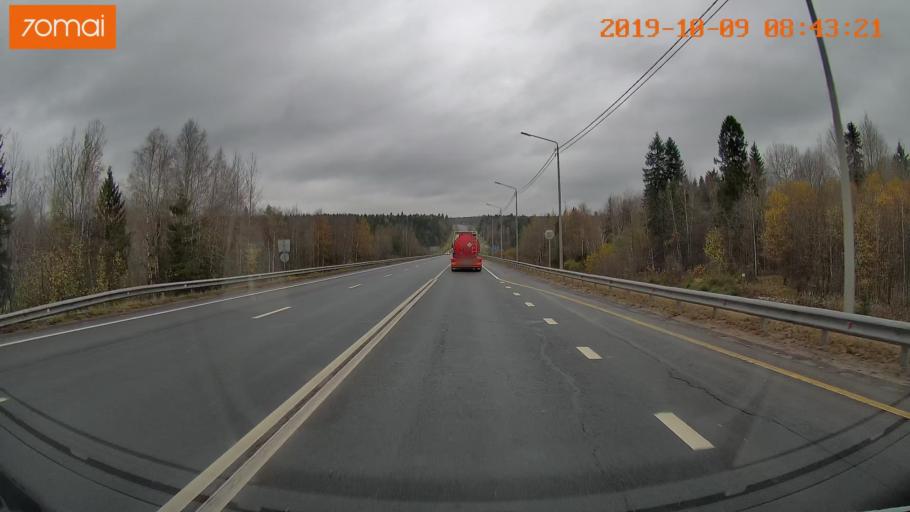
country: RU
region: Vologda
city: Gryazovets
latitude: 59.0233
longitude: 40.1147
